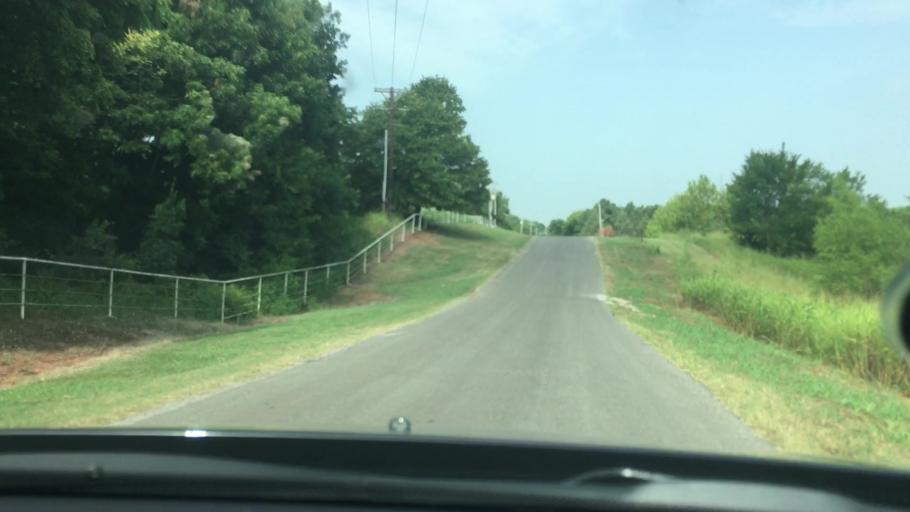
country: US
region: Oklahoma
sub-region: Garvin County
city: Pauls Valley
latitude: 34.7968
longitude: -97.1839
